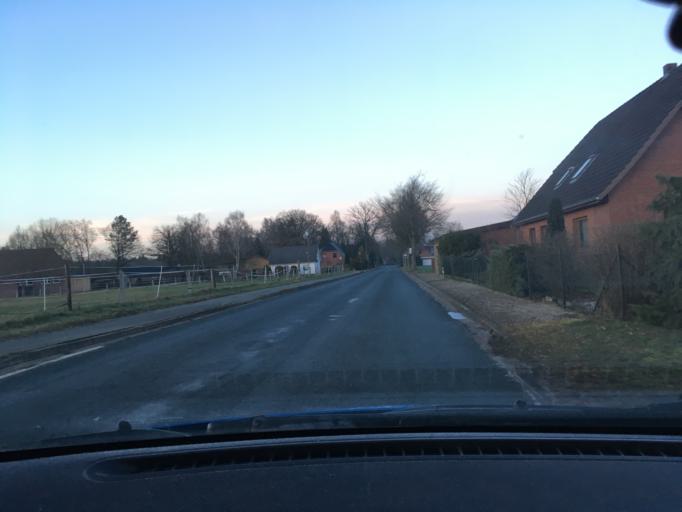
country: DE
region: Lower Saxony
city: Handeloh
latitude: 53.2602
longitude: 9.8820
